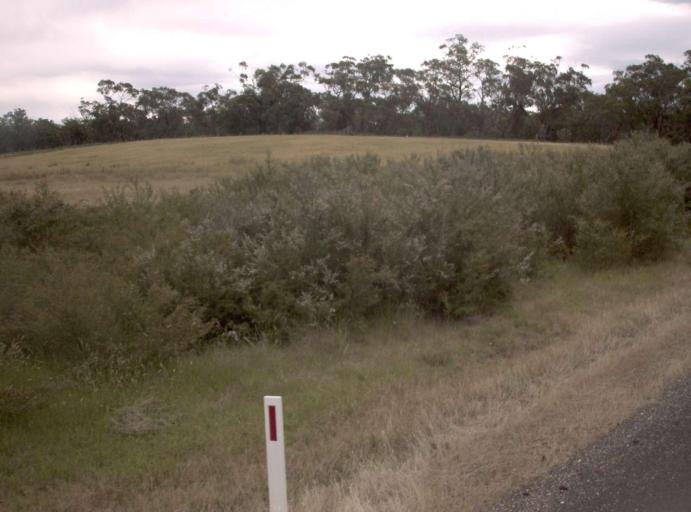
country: AU
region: Victoria
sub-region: Wellington
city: Sale
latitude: -38.2735
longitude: 147.0354
